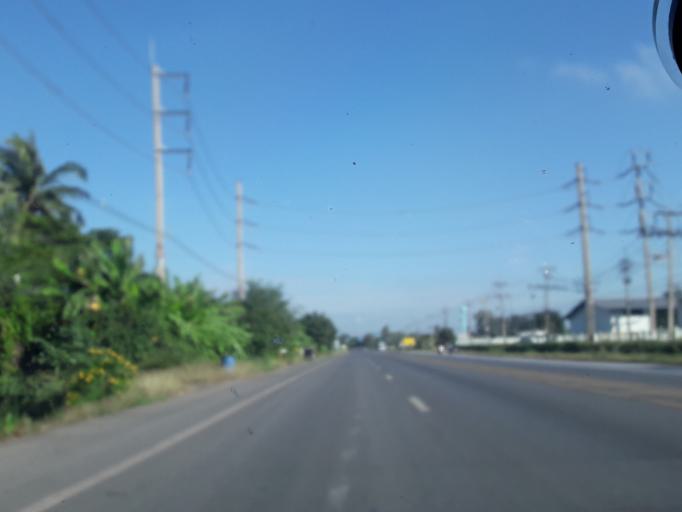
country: TH
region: Sara Buri
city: Phra Phutthabat
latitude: 14.8325
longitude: 100.8539
